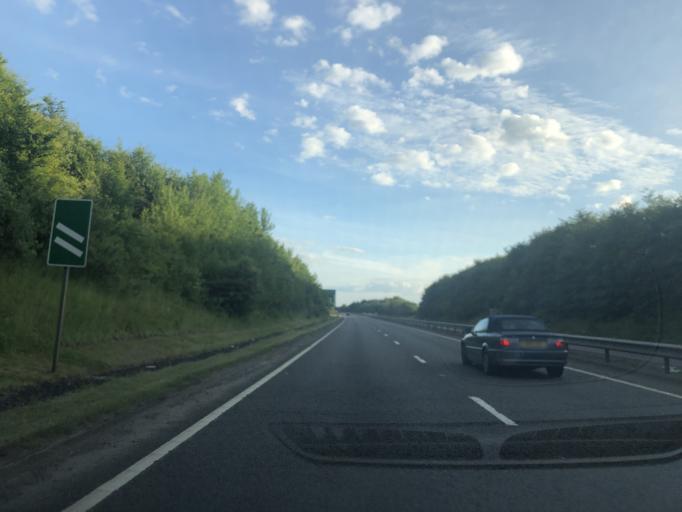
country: GB
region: Scotland
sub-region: Fife
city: Cowdenbeath
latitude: 56.1088
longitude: -3.3286
